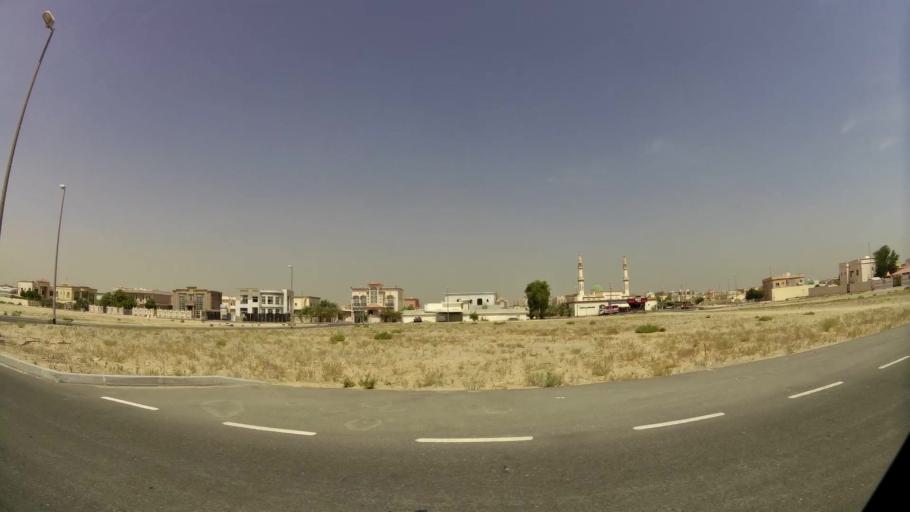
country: AE
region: Ash Shariqah
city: Sharjah
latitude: 25.1796
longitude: 55.4185
